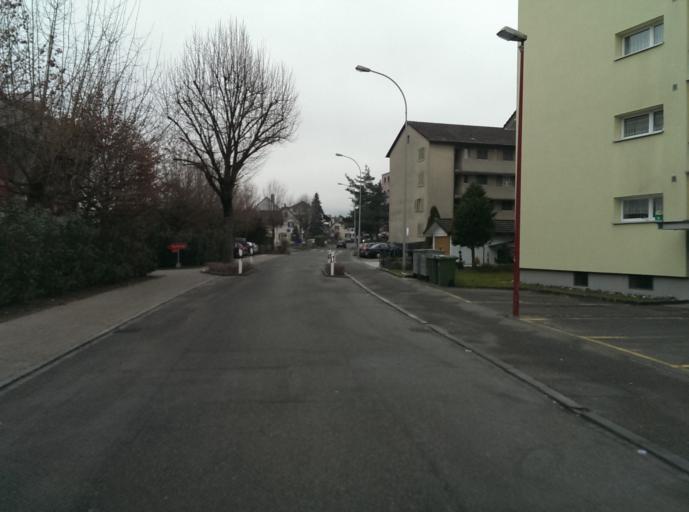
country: CH
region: Aargau
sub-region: Bezirk Baden
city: Neuenhof
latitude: 47.4502
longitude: 8.3309
